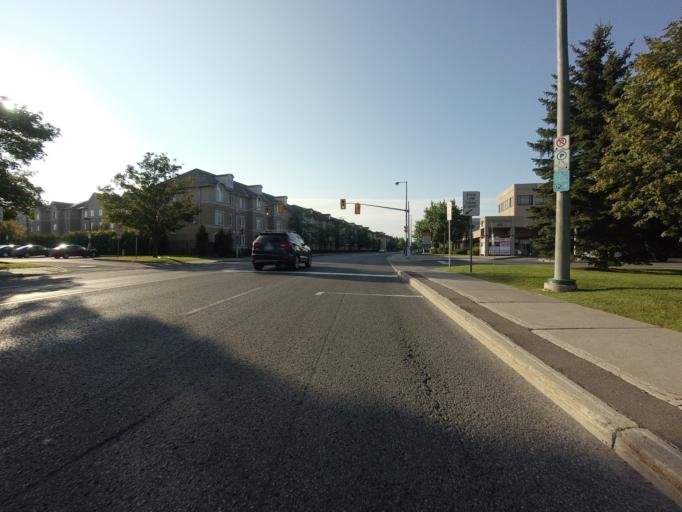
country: CA
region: Ontario
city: Bells Corners
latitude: 45.3421
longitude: -75.7624
